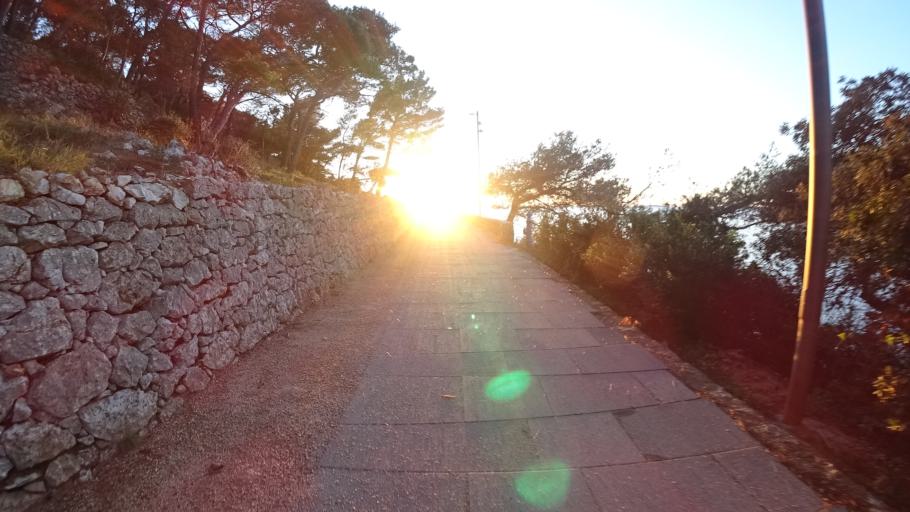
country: HR
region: Primorsko-Goranska
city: Mali Losinj
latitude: 44.5269
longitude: 14.4502
